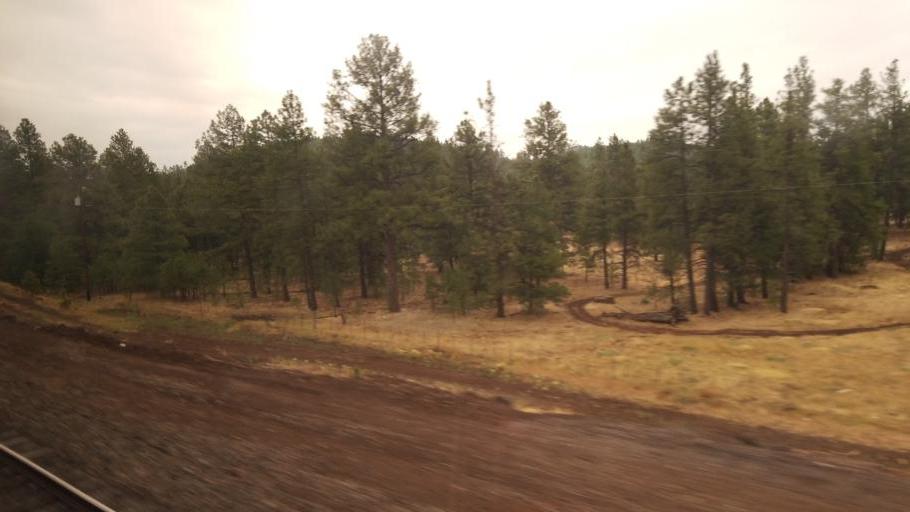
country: US
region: Arizona
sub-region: Coconino County
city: Parks
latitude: 35.2535
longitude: -111.9348
